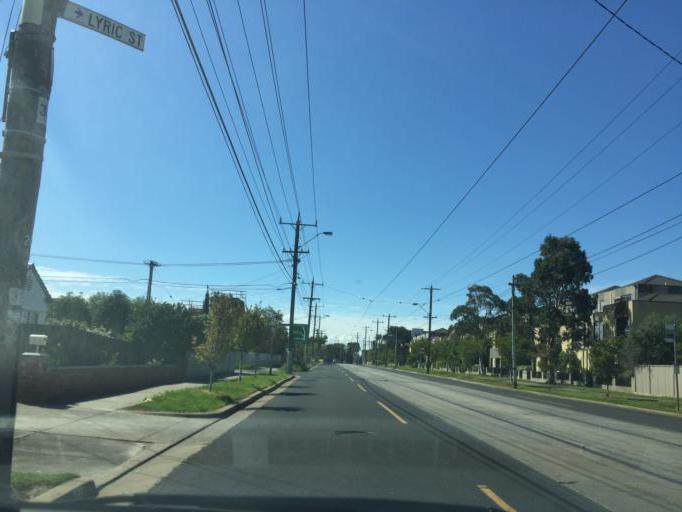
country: AU
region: Victoria
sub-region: Maribyrnong
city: Maribyrnong
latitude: -37.7823
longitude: 144.8911
